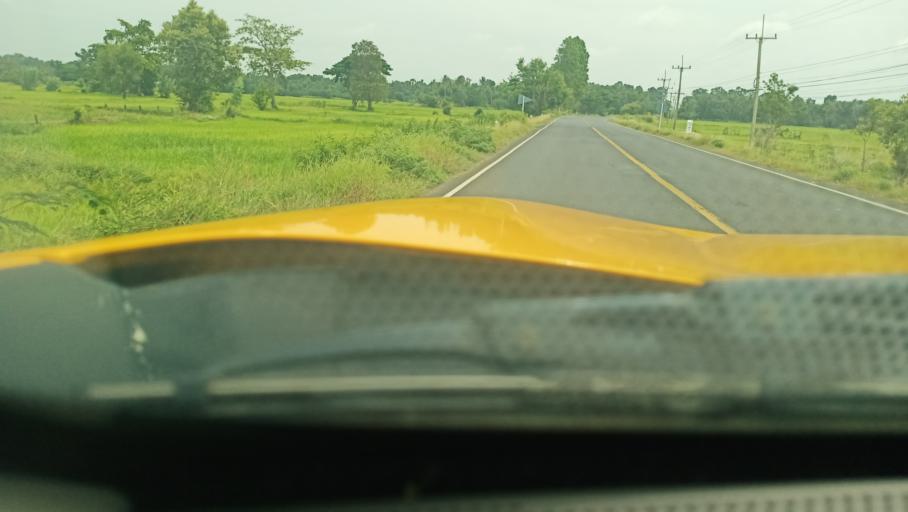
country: TH
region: Sisaket
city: Si Sa Ket
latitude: 15.2024
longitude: 104.2690
